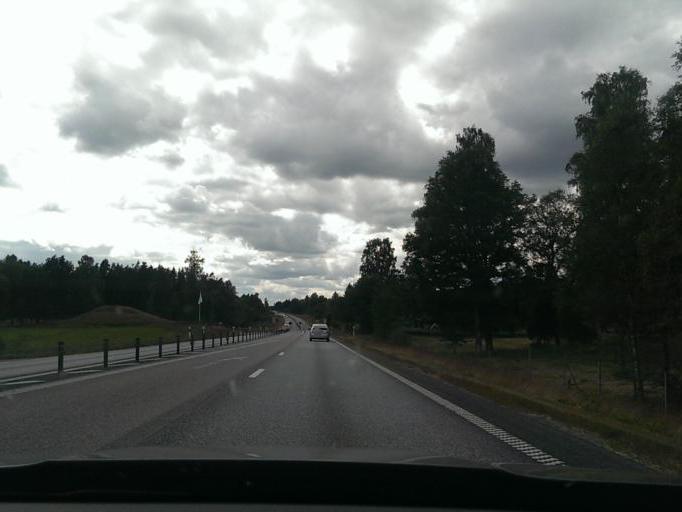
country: SE
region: Joenkoeping
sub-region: Varnamo Kommun
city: Varnamo
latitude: 57.1808
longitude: 13.9360
